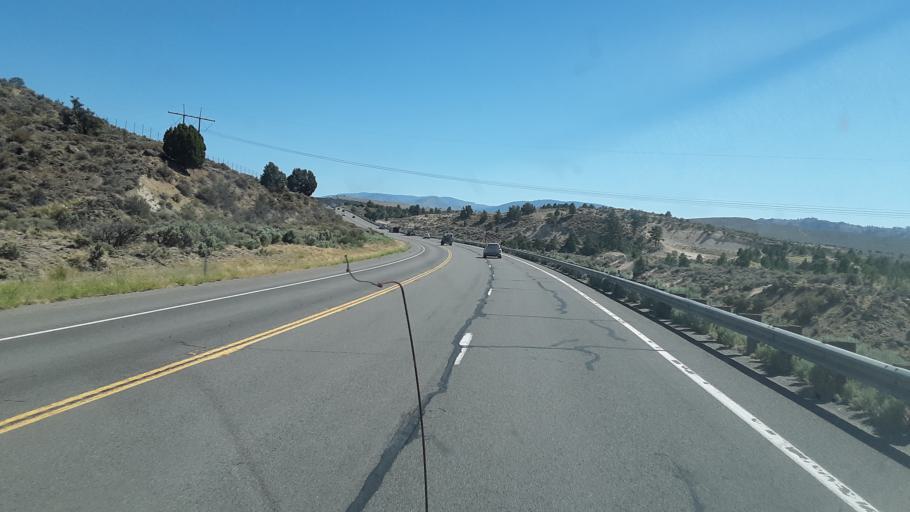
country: US
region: Nevada
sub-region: Washoe County
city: Cold Springs
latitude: 39.8644
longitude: -120.0397
